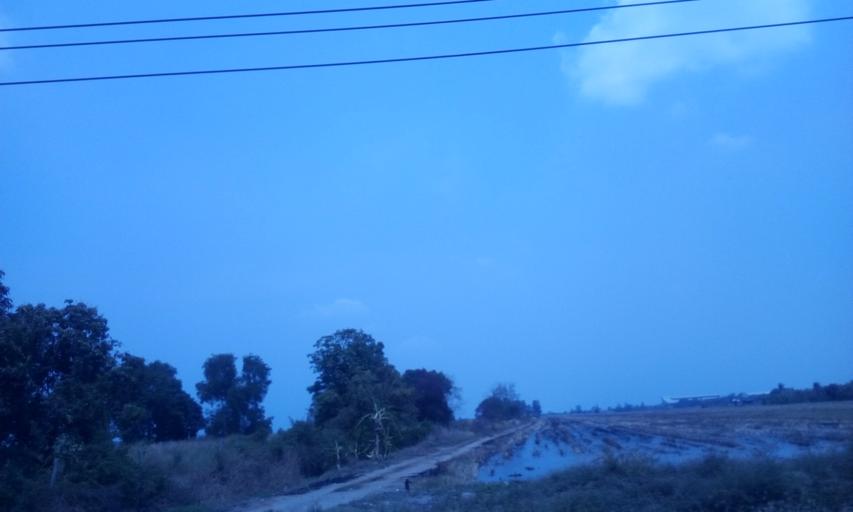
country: TH
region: Bangkok
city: Nong Chok
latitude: 13.9635
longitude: 100.9089
